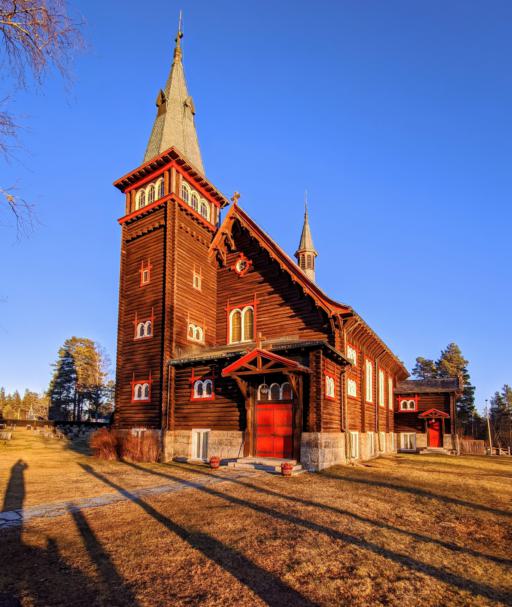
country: NO
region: Hedmark
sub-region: Amot
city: Rena
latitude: 61.3000
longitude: 11.7623
